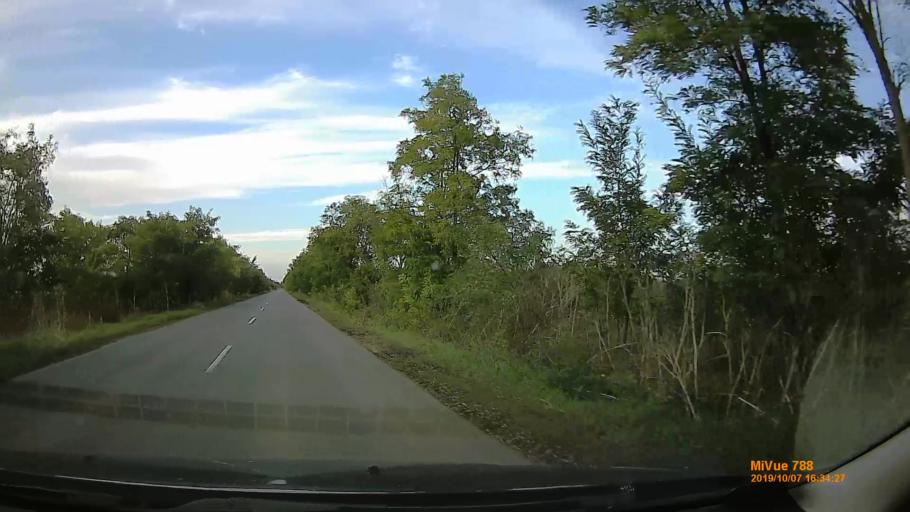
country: HU
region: Bekes
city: Szarvas
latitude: 46.8011
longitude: 20.6205
